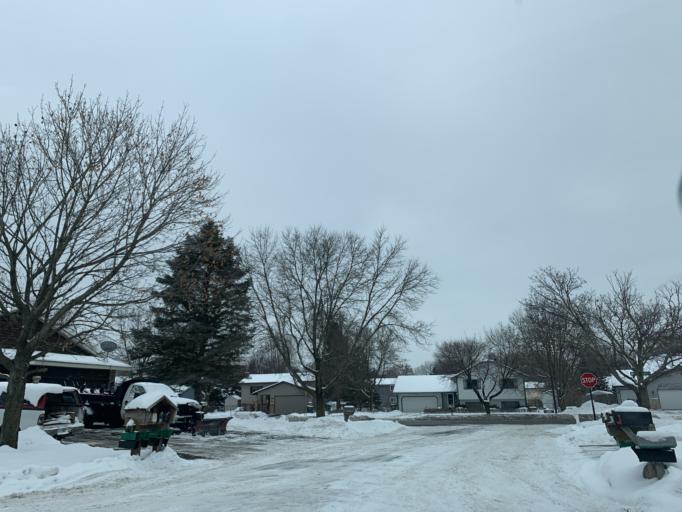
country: US
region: Minnesota
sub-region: Anoka County
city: Coon Rapids
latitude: 45.1622
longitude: -93.2997
